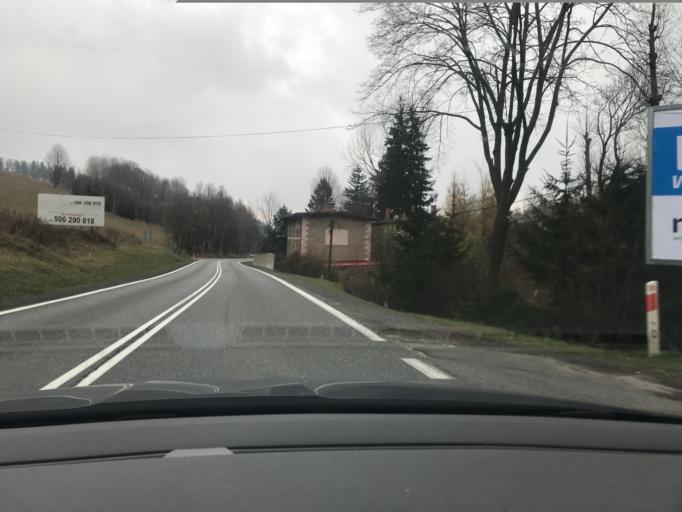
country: PL
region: Lower Silesian Voivodeship
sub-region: Powiat klodzki
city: Duszniki-Zdroj
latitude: 50.3940
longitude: 16.3680
